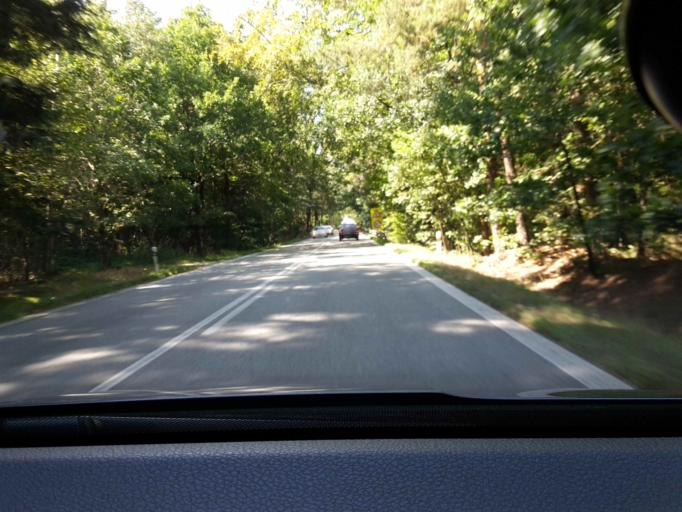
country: CZ
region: Jihocesky
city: Kardasova Recice
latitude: 49.1749
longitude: 14.8855
